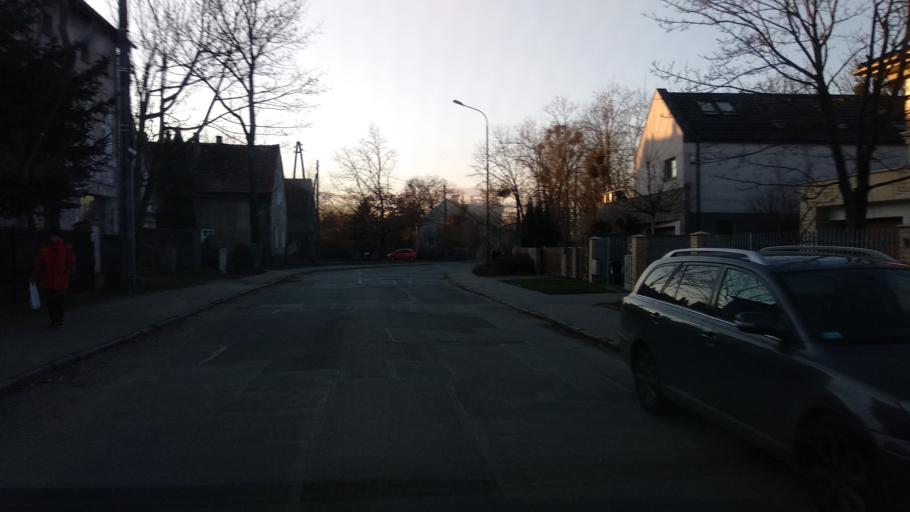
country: PL
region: Lower Silesian Voivodeship
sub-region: Powiat wroclawski
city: Radwanice
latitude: 51.0619
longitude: 17.0782
